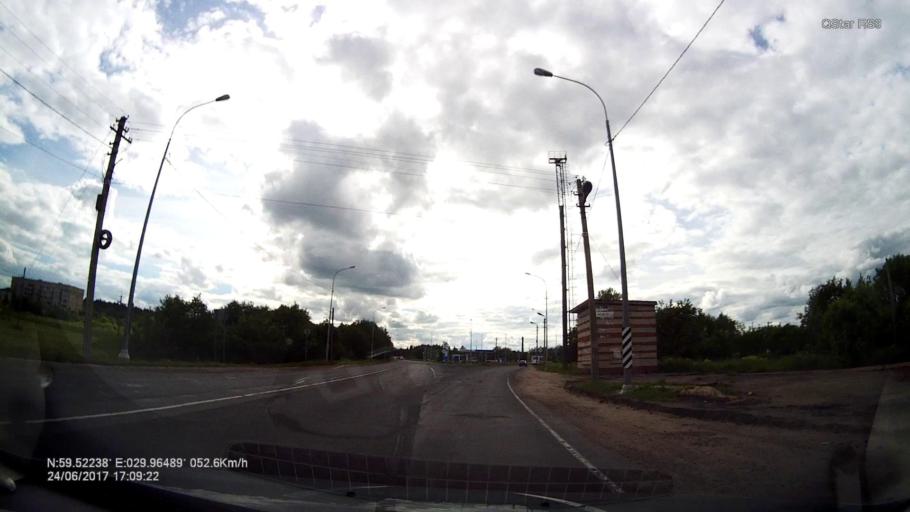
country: RU
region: Leningrad
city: Voyskovitsy
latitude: 59.5224
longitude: 29.9645
